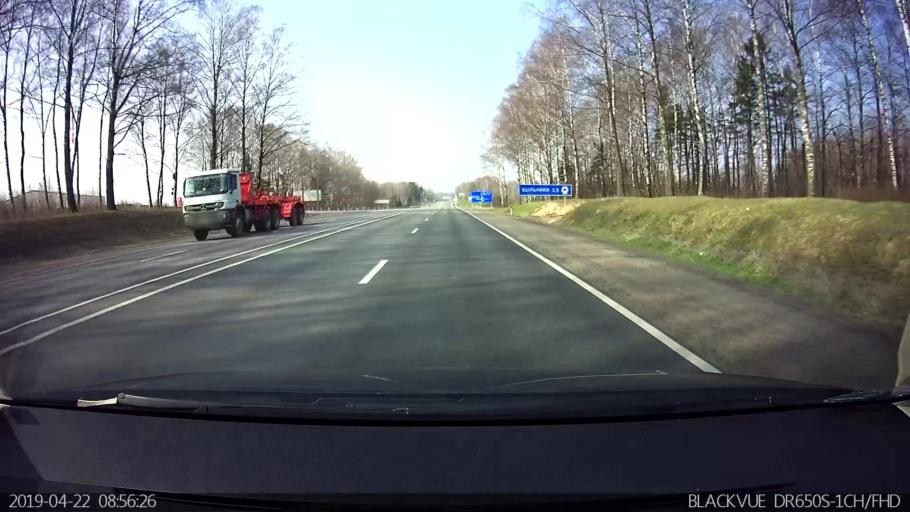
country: RU
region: Smolensk
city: Pechersk
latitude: 54.8746
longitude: 32.0387
